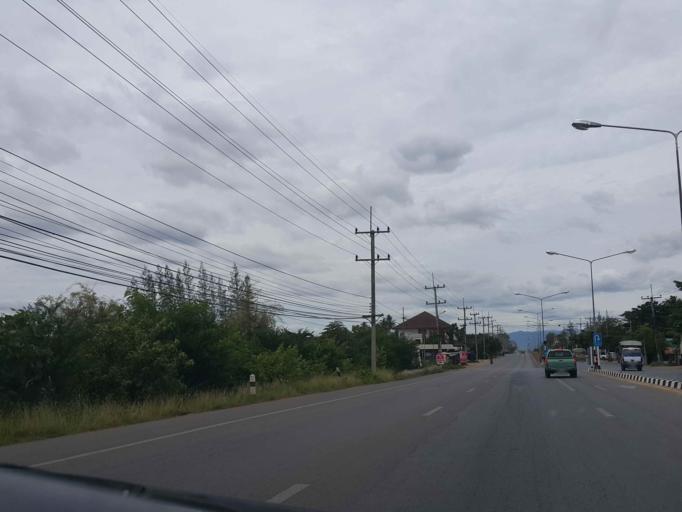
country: TH
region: Chiang Mai
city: Doi Lo
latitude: 18.5156
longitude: 98.8423
